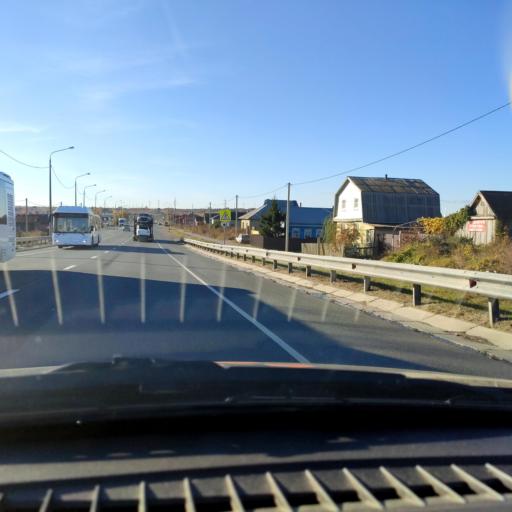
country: RU
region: Samara
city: Mezhdurechensk
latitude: 53.2480
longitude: 49.1811
